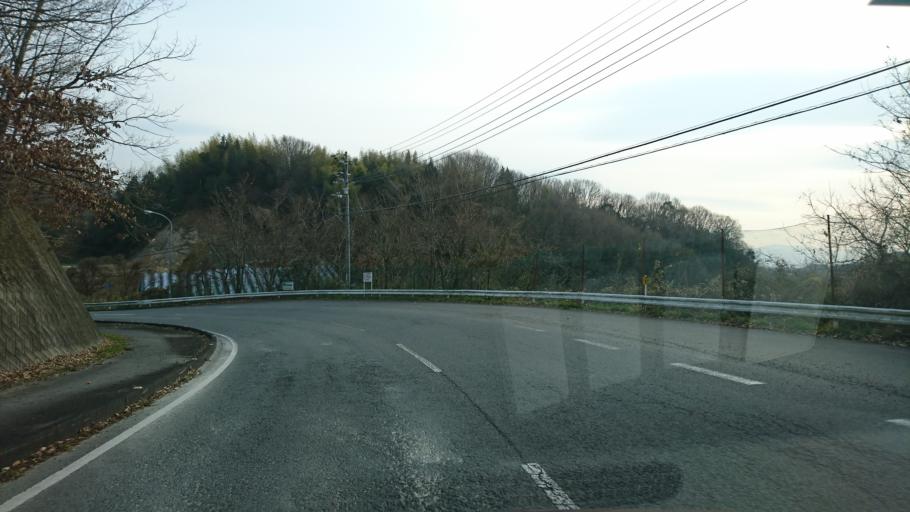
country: JP
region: Ehime
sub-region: Shikoku-chuo Shi
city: Matsuyama
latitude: 33.8970
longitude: 132.8058
